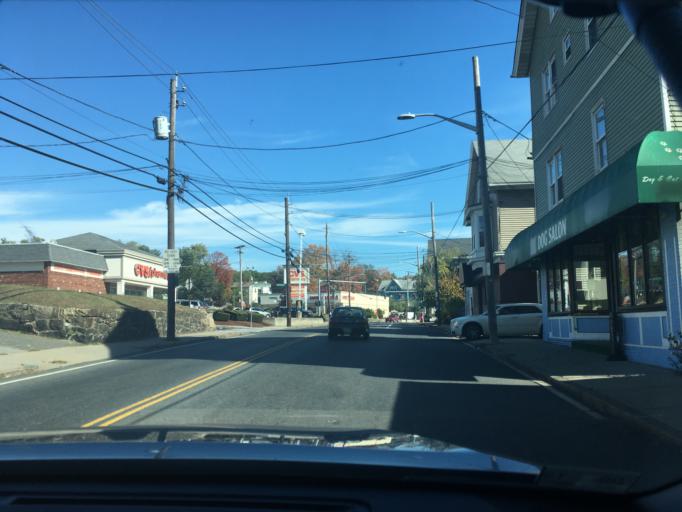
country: US
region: Rhode Island
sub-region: Providence County
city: North Providence
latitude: 41.8336
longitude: -71.4690
